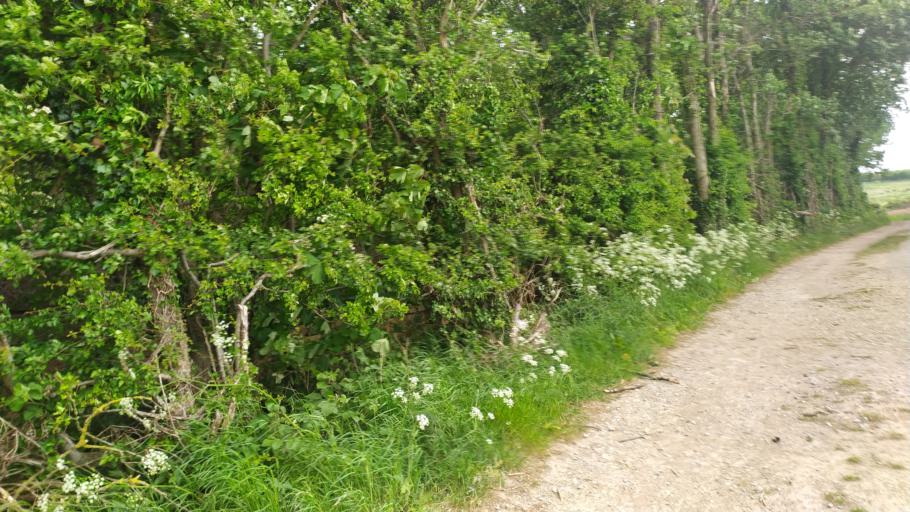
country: GB
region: England
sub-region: City and Borough of Leeds
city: Thorner
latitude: 53.8647
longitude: -1.3970
